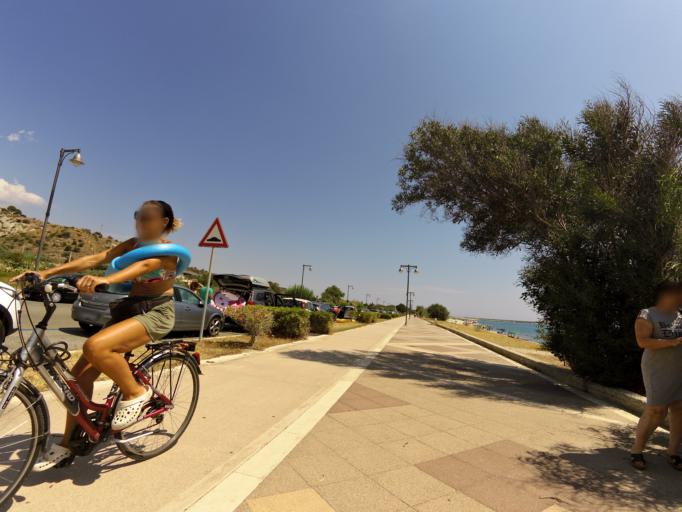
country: IT
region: Calabria
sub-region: Provincia di Reggio Calabria
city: Roccella Ionica
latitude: 38.3250
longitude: 16.4183
